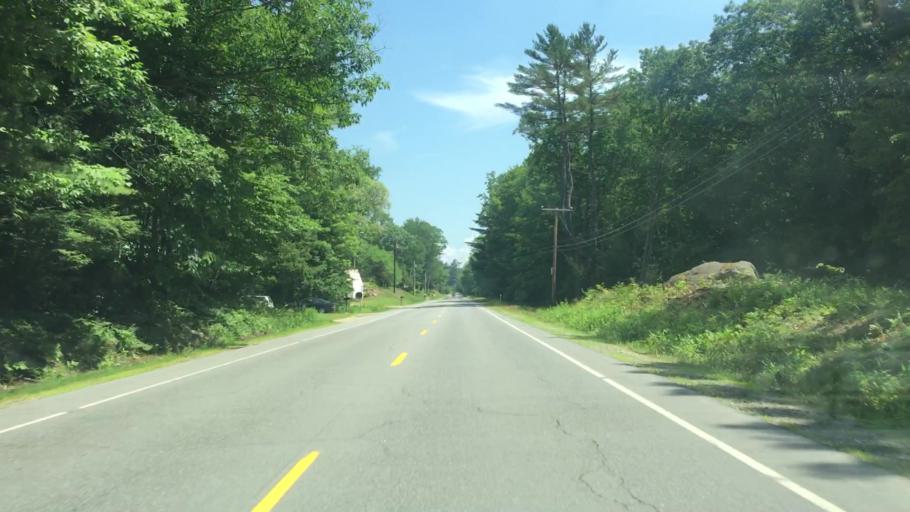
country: US
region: New Hampshire
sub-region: Sullivan County
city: Newport
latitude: 43.4205
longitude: -72.1753
